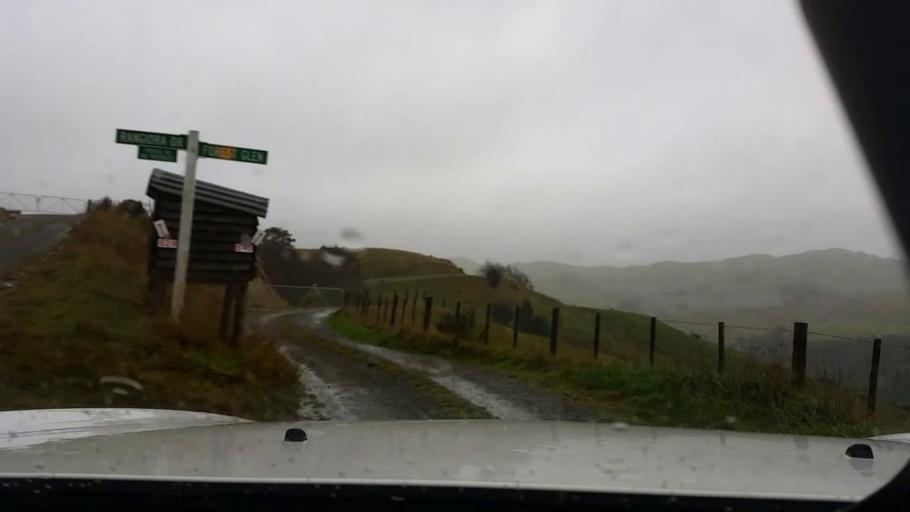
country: NZ
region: Wellington
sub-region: Masterton District
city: Masterton
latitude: -41.2072
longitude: 175.8142
